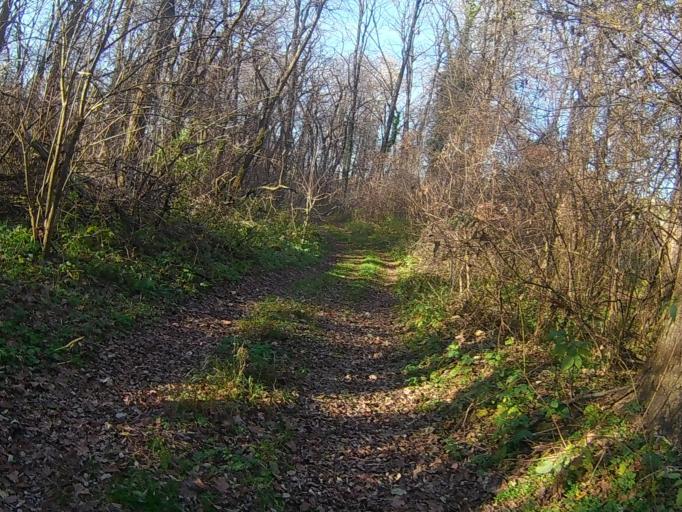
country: SI
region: Duplek
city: Zgornji Duplek
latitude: 46.5101
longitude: 15.7202
